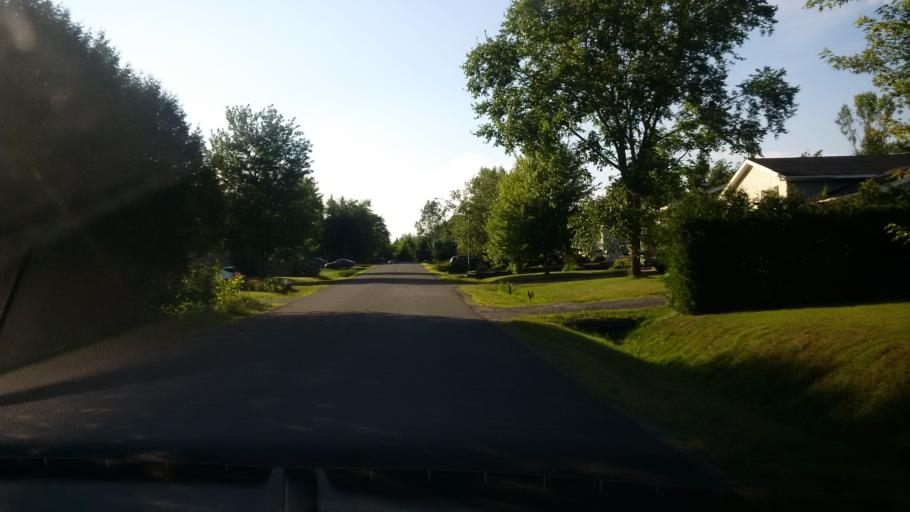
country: CA
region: New Brunswick
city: Fredericton
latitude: 45.8888
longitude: -66.6899
